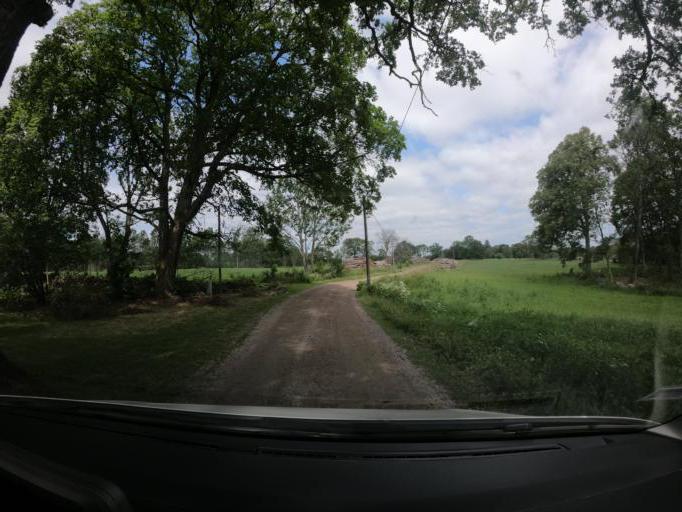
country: SE
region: Skane
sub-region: Hoors Kommun
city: Hoeoer
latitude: 56.0429
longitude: 13.5521
